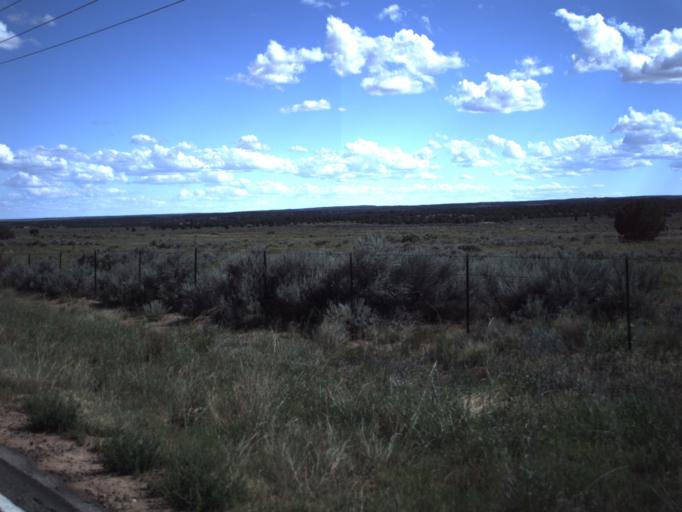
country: US
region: Arizona
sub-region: Mohave County
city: Colorado City
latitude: 37.0458
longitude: -113.0860
